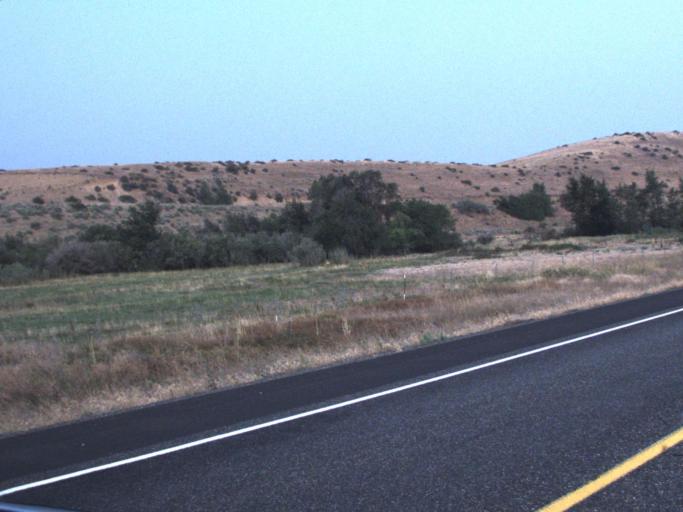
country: US
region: Washington
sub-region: Kittitas County
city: Ellensburg
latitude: 47.0495
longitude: -120.6105
